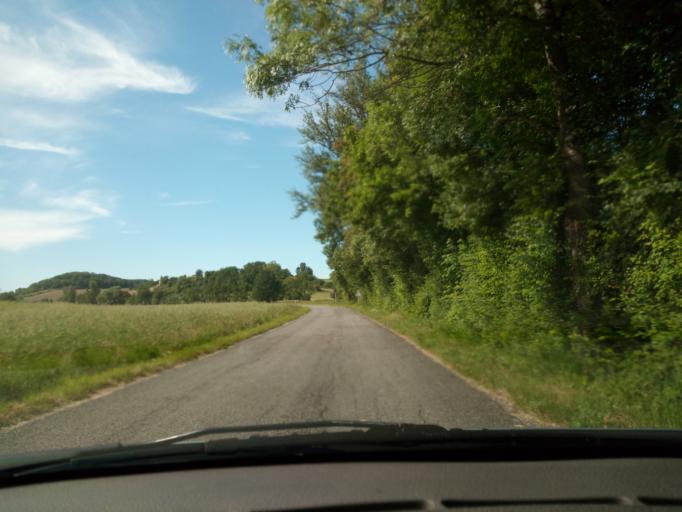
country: FR
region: Midi-Pyrenees
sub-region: Departement du Tarn-et-Garonne
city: Molieres
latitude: 44.2270
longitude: 1.3295
